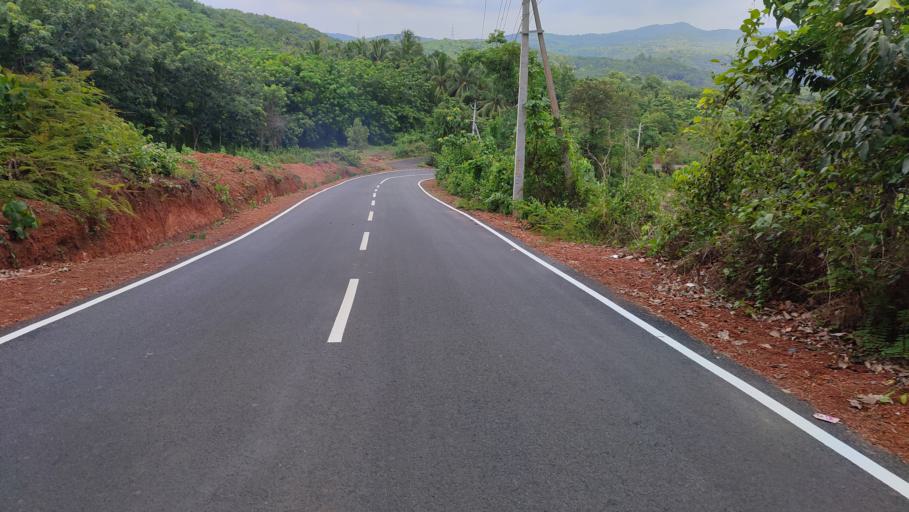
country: IN
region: Kerala
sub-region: Kasaragod District
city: Kannangad
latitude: 12.3206
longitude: 75.1529
